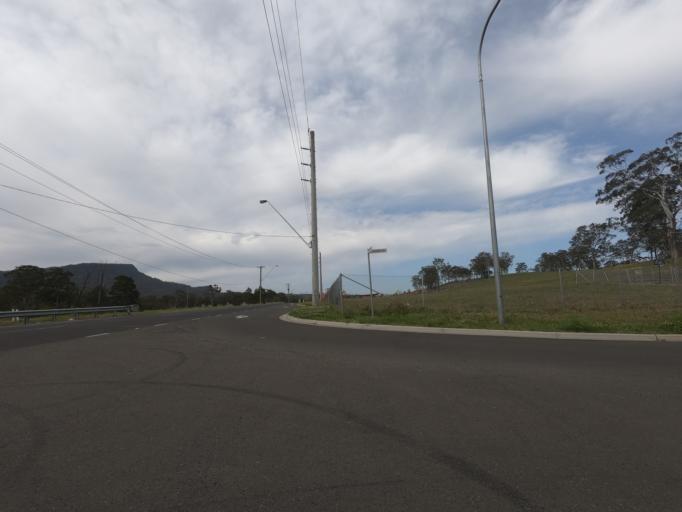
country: AU
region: New South Wales
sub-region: Wollongong
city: Dapto
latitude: -34.4788
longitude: 150.7830
